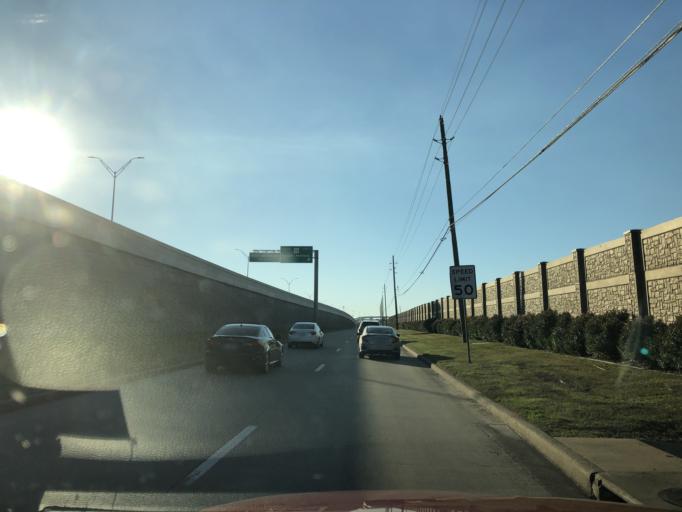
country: US
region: Texas
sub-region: Fort Bend County
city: Cinco Ranch
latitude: 29.7016
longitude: -95.7616
